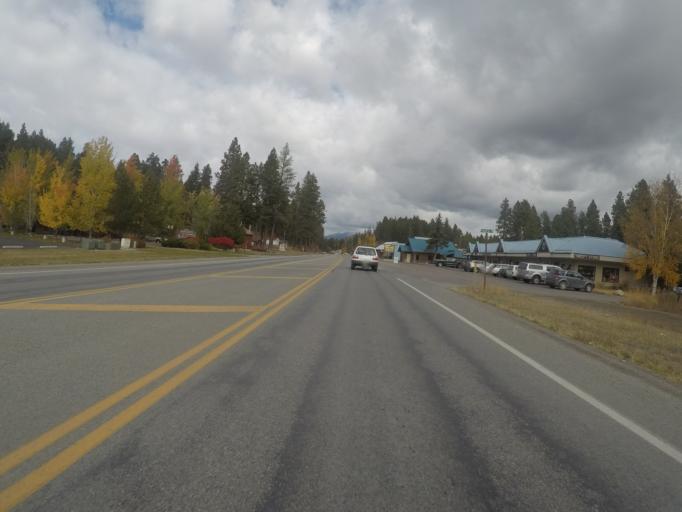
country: US
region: Montana
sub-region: Flathead County
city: Bigfork
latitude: 48.0768
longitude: -114.0786
